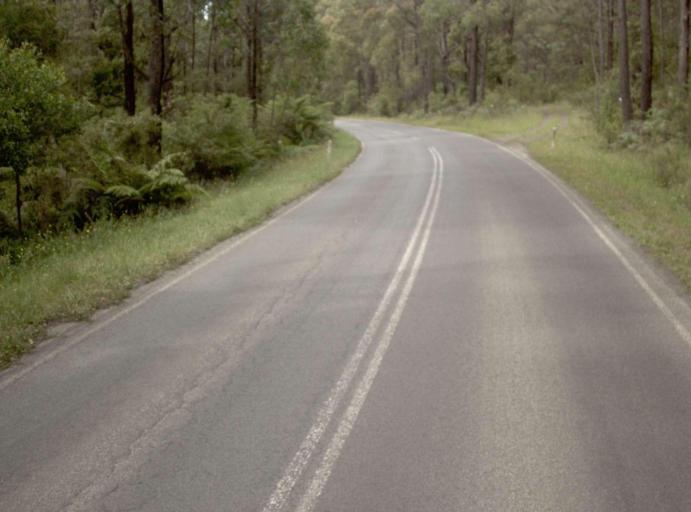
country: AU
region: Victoria
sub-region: Latrobe
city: Traralgon
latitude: -38.0954
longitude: 146.4404
